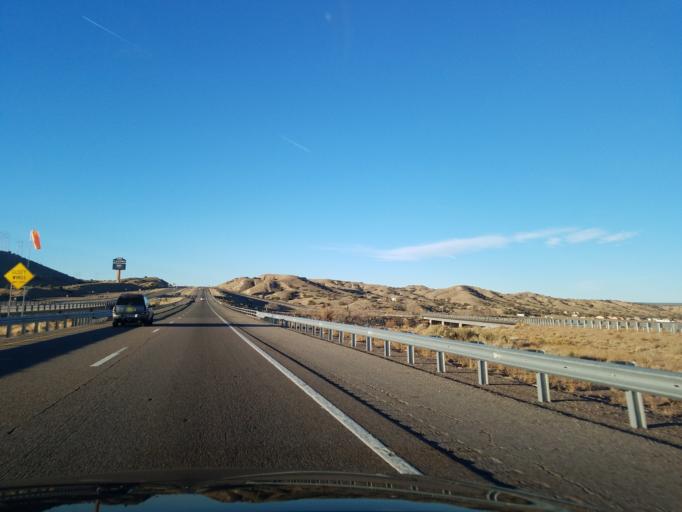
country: US
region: New Mexico
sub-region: Sandoval County
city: San Felipe Pueblo
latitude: 35.4195
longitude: -106.4020
